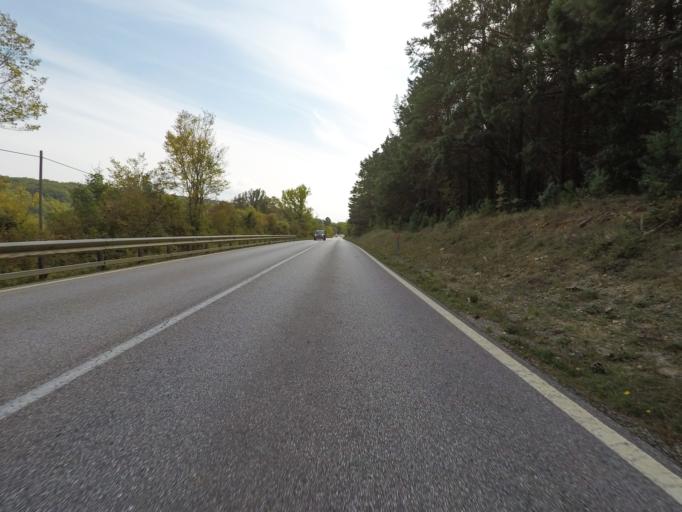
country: IT
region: Tuscany
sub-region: Provincia di Siena
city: Murlo
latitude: 43.1315
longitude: 11.2928
